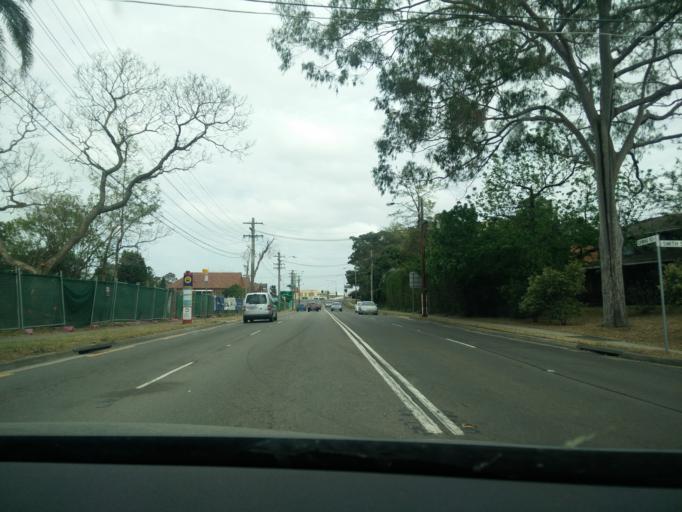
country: AU
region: New South Wales
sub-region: Parramatta
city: Epping
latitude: -33.7739
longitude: 151.0853
